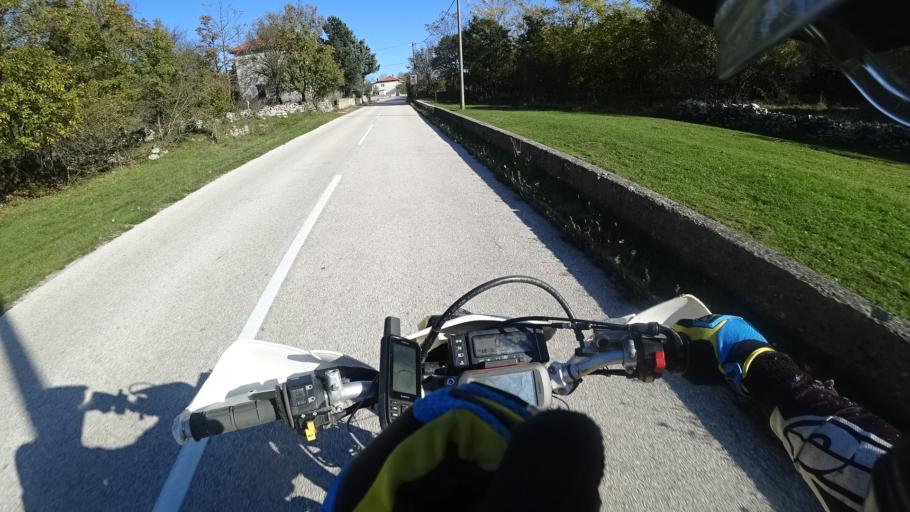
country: HR
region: Primorsko-Goranska
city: Klana
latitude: 45.4452
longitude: 14.3339
